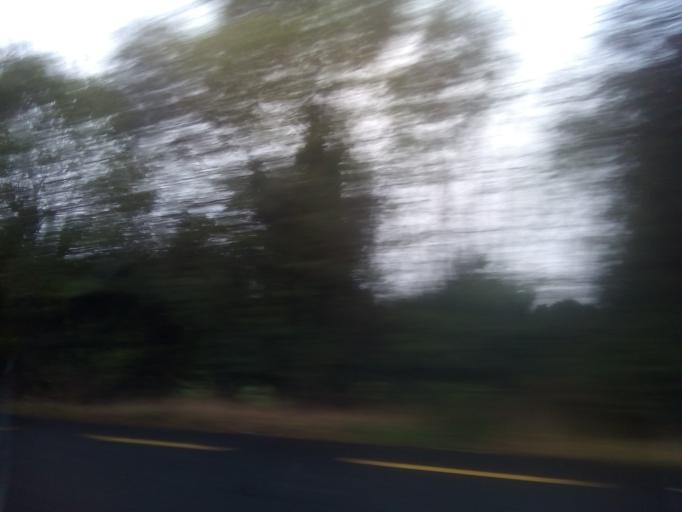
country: IE
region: Leinster
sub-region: An Longfort
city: Edgeworthstown
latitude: 53.7039
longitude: -7.6603
